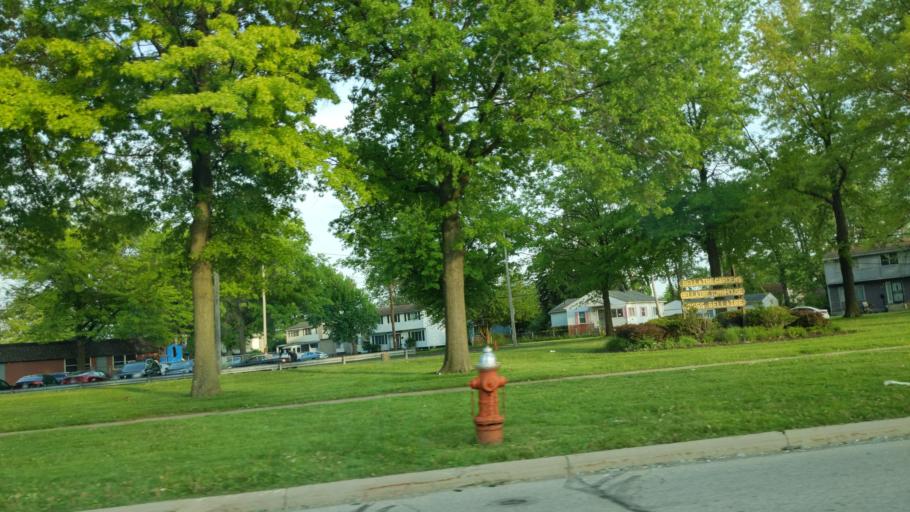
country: US
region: Ohio
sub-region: Cuyahoga County
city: Brooklyn
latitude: 41.4406
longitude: -81.7755
